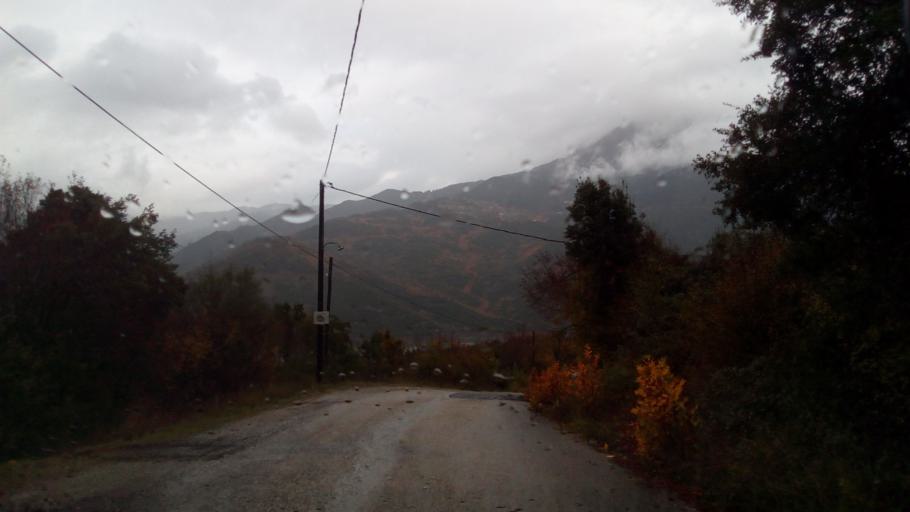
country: GR
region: West Greece
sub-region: Nomos Aitolias kai Akarnanias
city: Thermo
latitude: 38.6560
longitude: 21.8532
